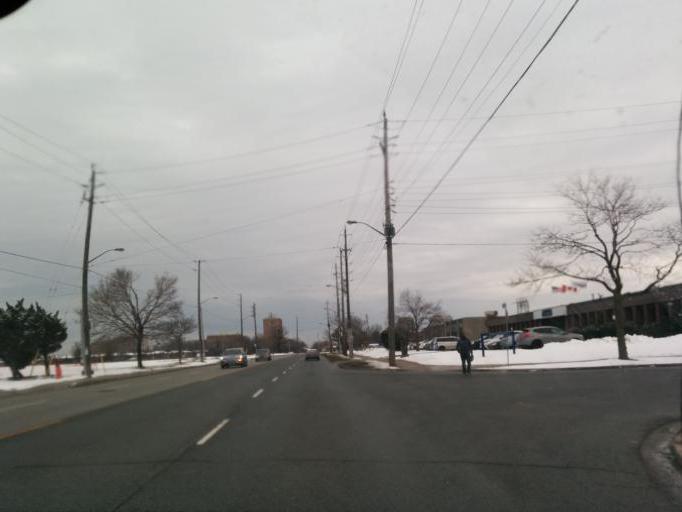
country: CA
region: Ontario
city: Etobicoke
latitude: 43.7383
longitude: -79.6185
